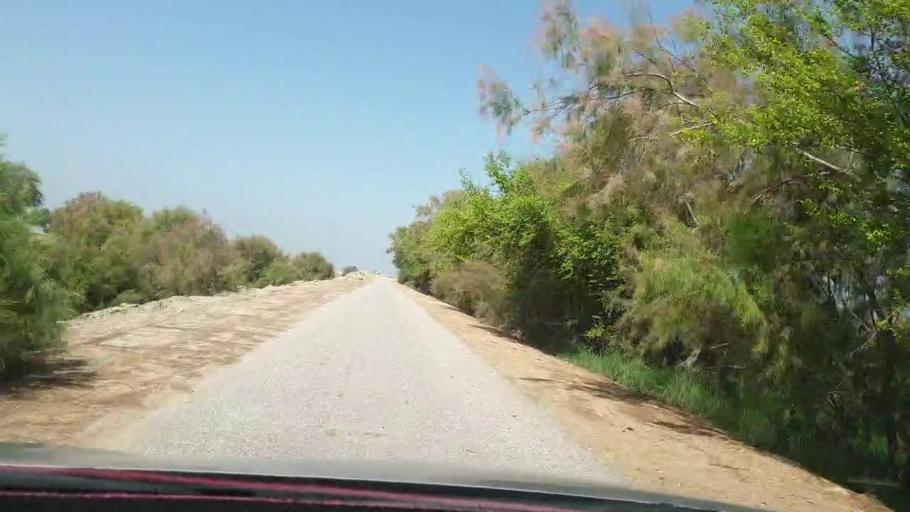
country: PK
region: Sindh
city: Warah
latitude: 27.5602
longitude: 67.7406
